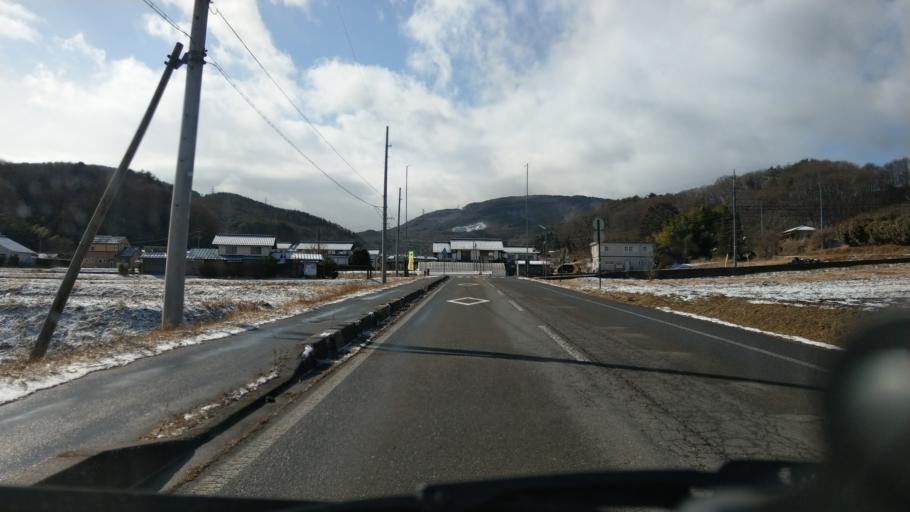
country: JP
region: Nagano
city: Kamimaruko
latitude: 36.2692
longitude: 138.3188
